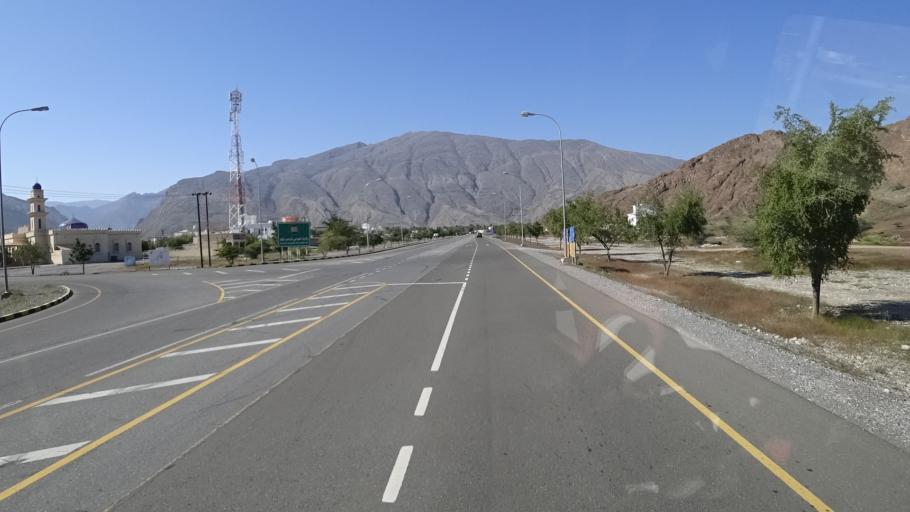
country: OM
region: Al Batinah
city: Bayt al `Awabi
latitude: 23.3177
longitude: 57.5400
